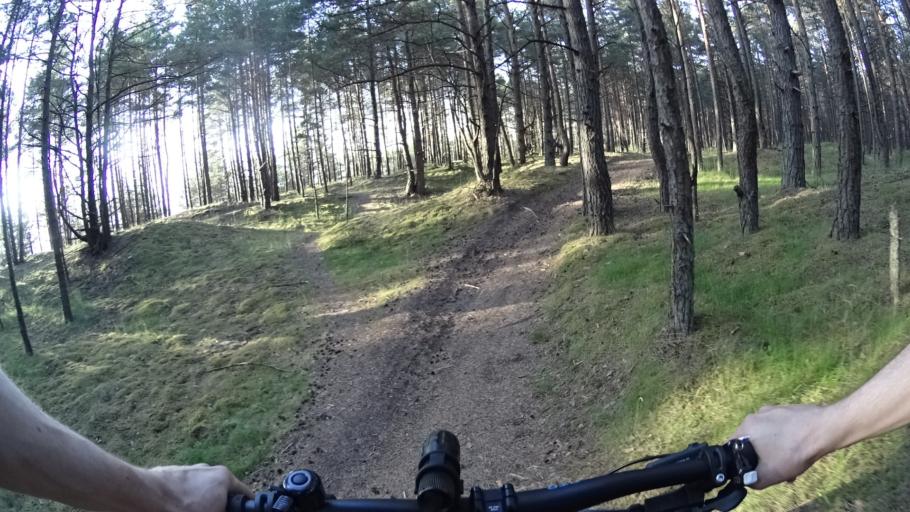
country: LV
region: Riga
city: Jaunciems
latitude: 57.1024
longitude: 24.1668
